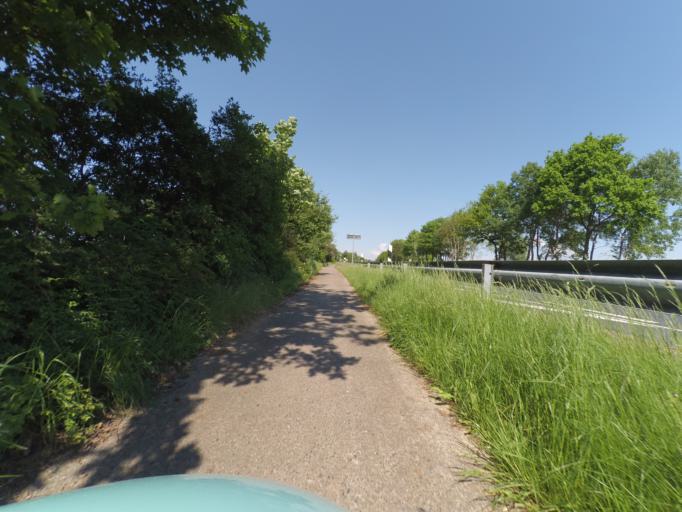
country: DE
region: Lower Saxony
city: Burgdorf
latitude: 52.4437
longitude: 9.9405
